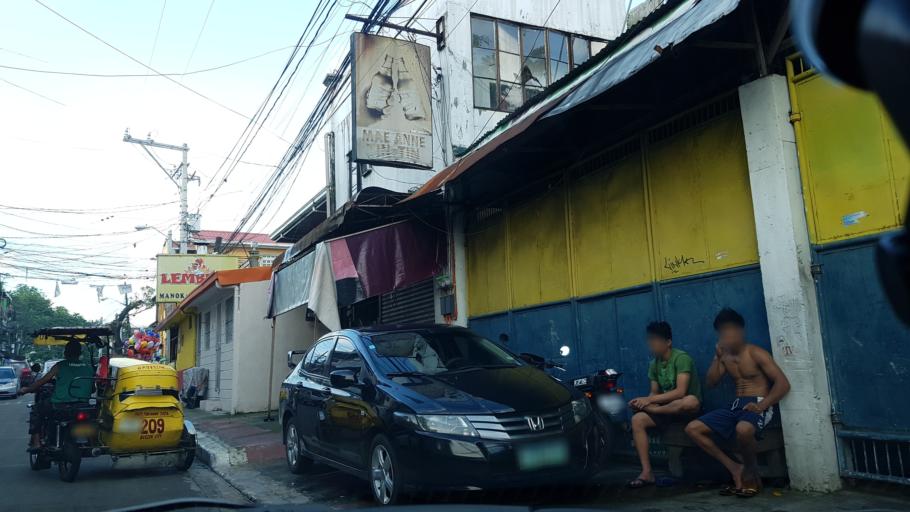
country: PH
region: Metro Manila
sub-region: Quezon City
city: Quezon City
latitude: 14.6388
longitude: 121.0517
